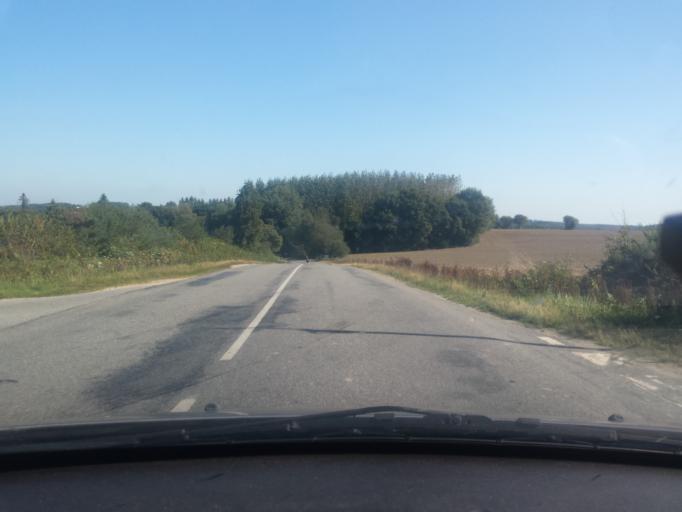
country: FR
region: Brittany
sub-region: Departement du Morbihan
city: Cleguerec
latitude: 48.1027
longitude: -3.1067
